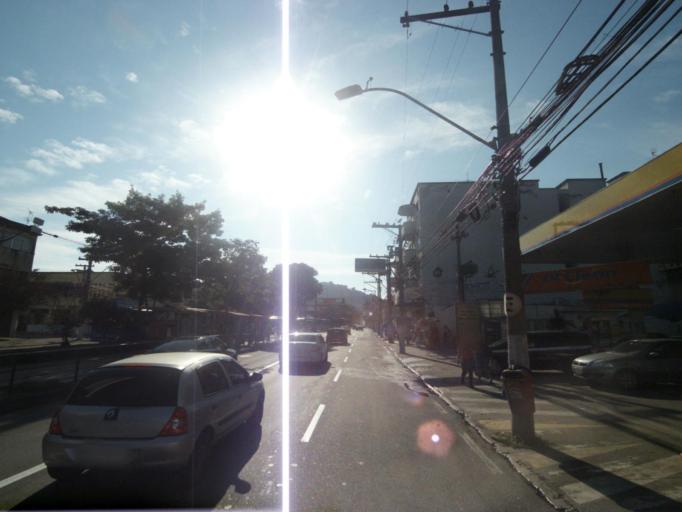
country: BR
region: Rio de Janeiro
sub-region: Niteroi
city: Niteroi
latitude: -22.8815
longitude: -43.0844
